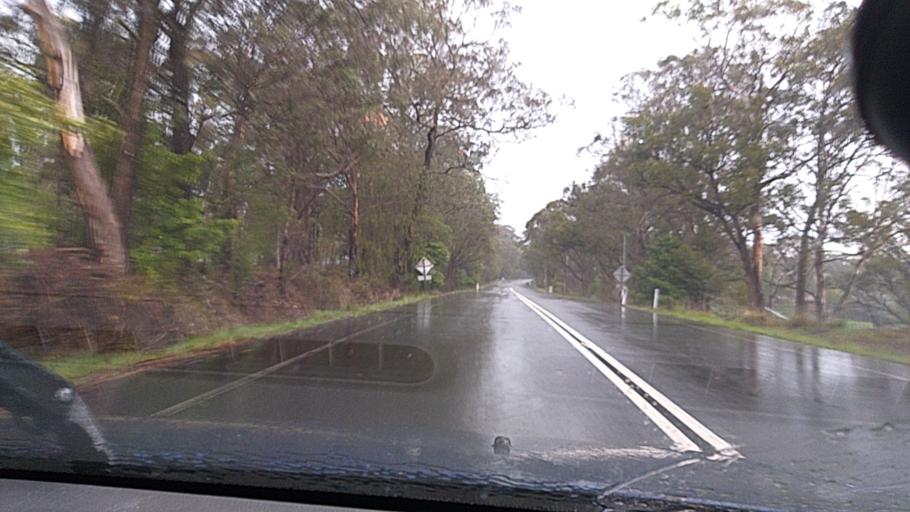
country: AU
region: New South Wales
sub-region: Wollondilly
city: Douglas Park
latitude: -34.2422
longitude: 150.7278
